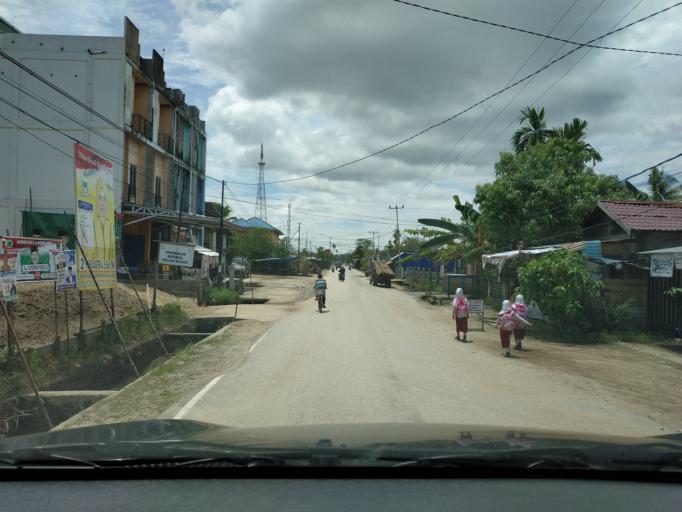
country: ID
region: Riau
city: Tembilahan
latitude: -0.3180
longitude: 103.1668
